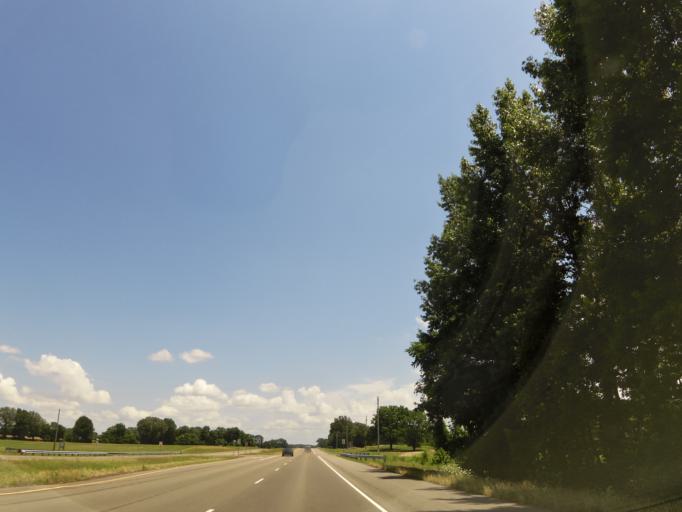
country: US
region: Tennessee
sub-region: Crockett County
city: Alamo
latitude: 35.8633
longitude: -89.2084
